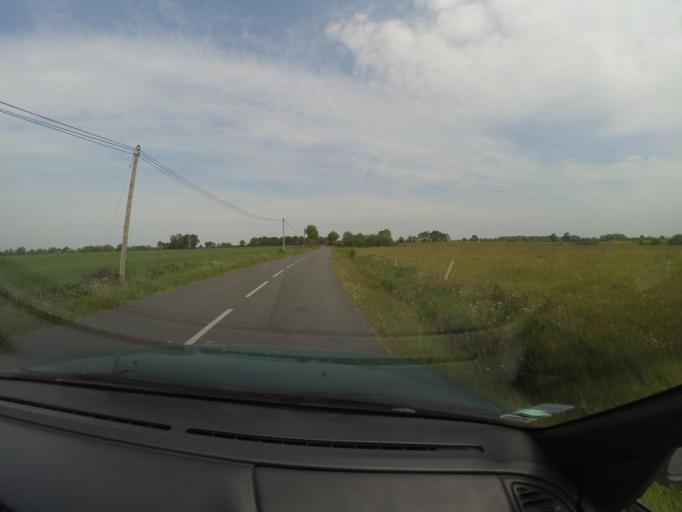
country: FR
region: Pays de la Loire
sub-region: Departement de la Loire-Atlantique
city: Saint-Lumine-de-Clisson
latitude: 47.0592
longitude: -1.3348
